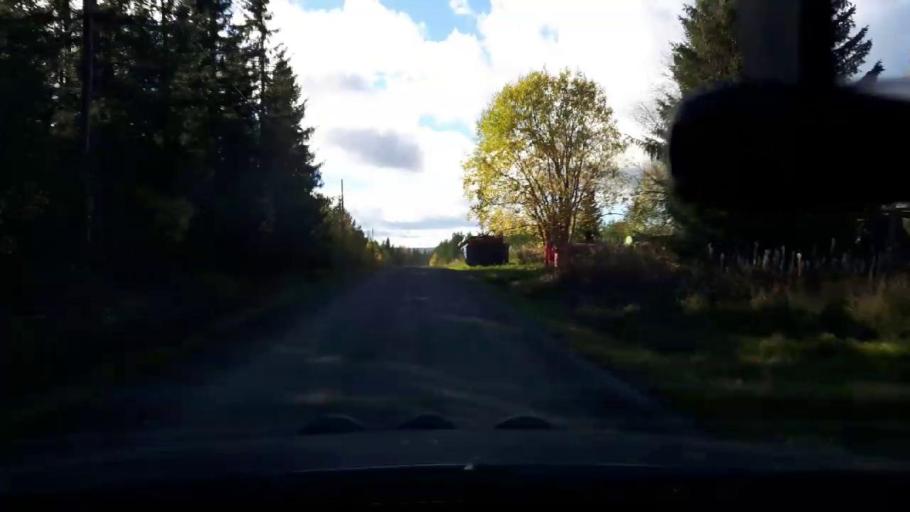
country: SE
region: Jaemtland
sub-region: Bergs Kommun
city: Hoverberg
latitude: 63.0221
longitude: 14.3277
